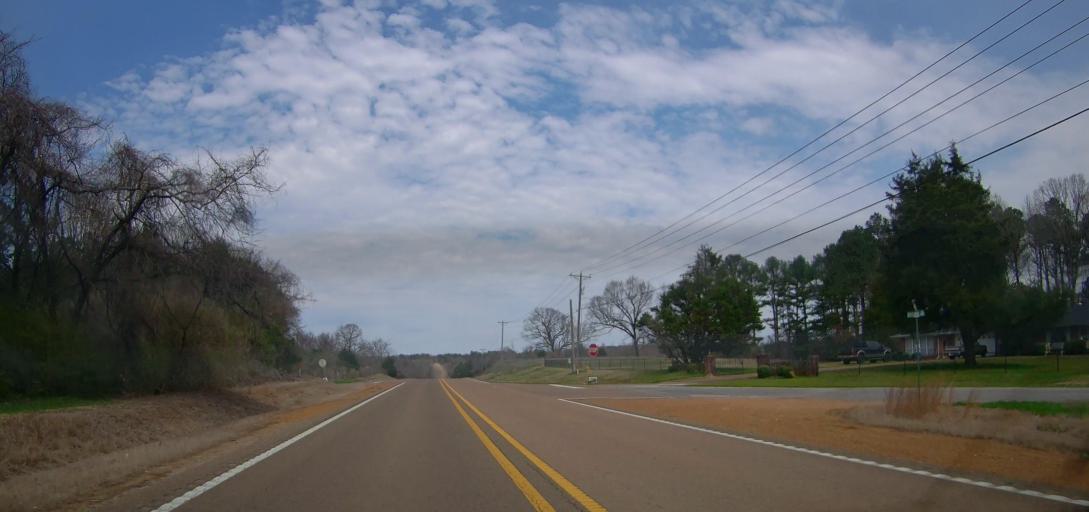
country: US
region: Mississippi
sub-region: Marshall County
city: Holly Springs
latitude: 34.7380
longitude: -89.4237
